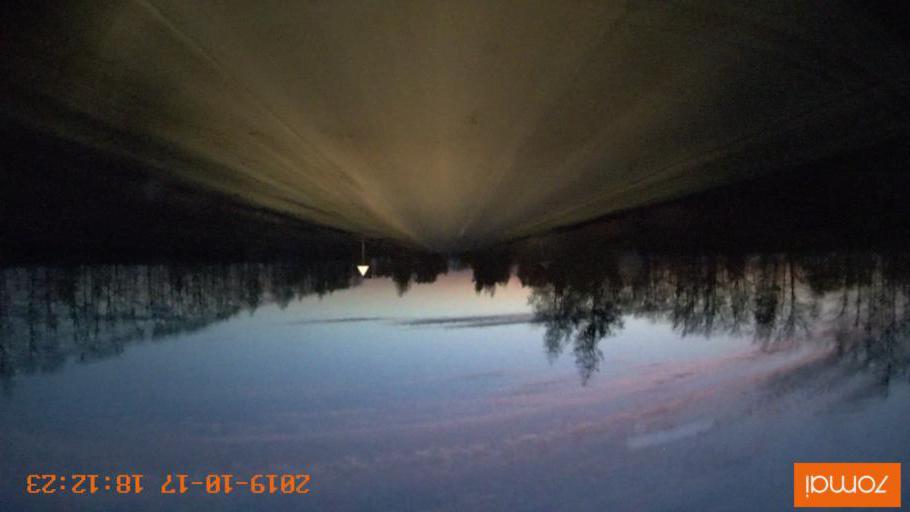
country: RU
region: Tula
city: Kurkino
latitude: 53.4119
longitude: 38.6134
